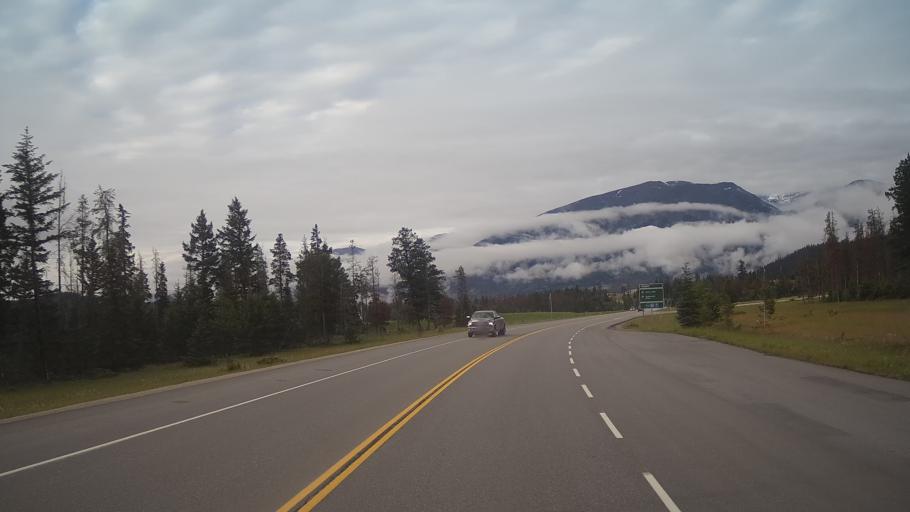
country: CA
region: Alberta
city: Jasper Park Lodge
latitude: 52.8984
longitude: -118.0668
